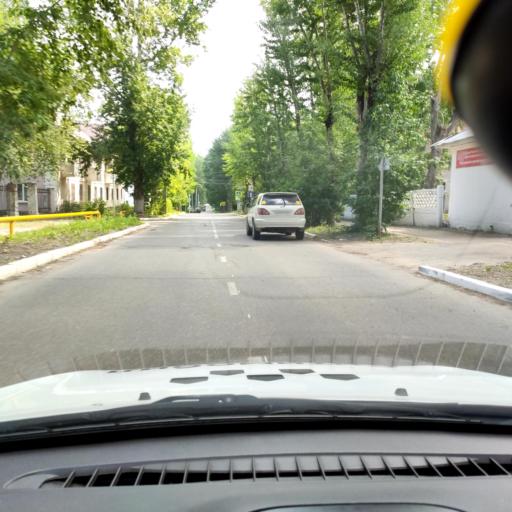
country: RU
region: Samara
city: Zhigulevsk
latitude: 53.3993
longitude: 49.4929
